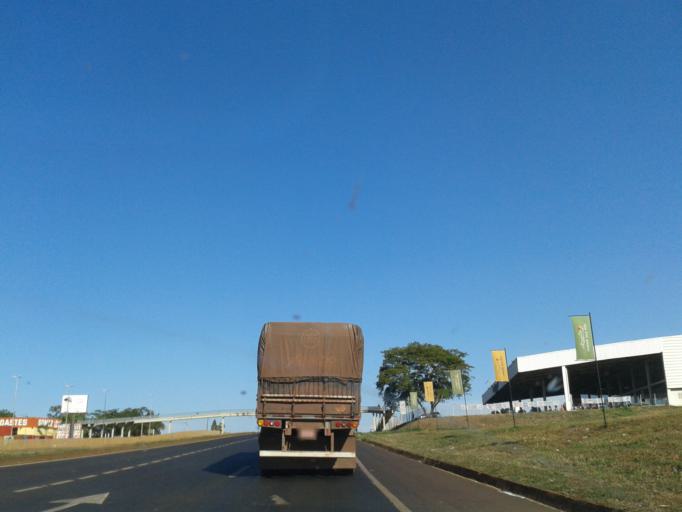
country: BR
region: Goias
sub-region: Itumbiara
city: Itumbiara
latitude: -18.4258
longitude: -49.1939
